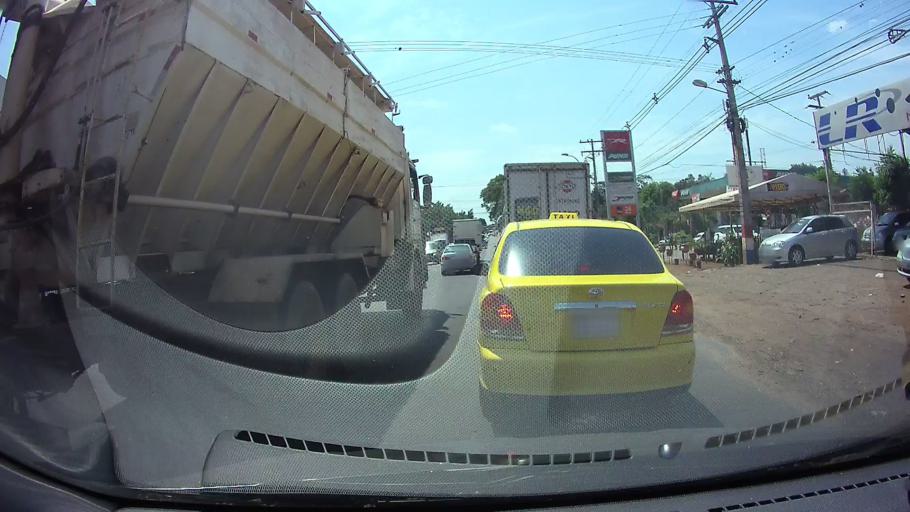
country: PY
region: Central
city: Capiata
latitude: -25.3929
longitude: -57.4683
